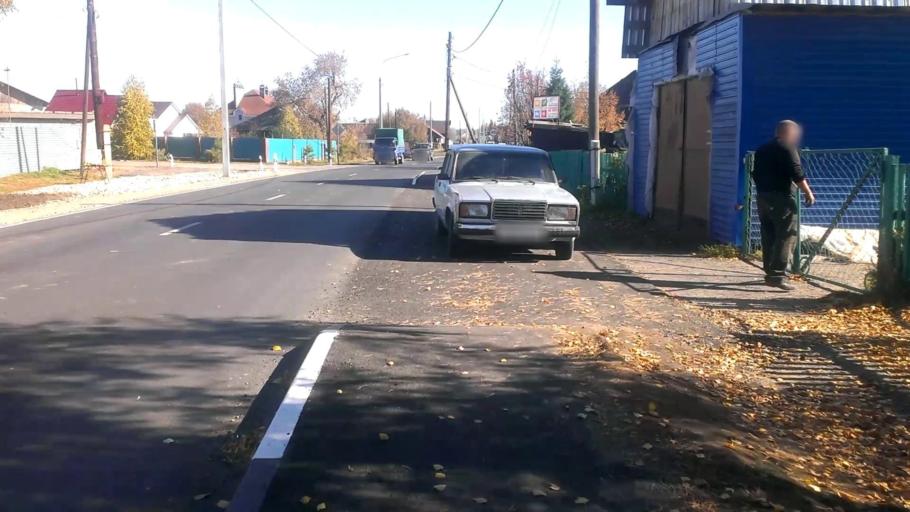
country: RU
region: Altai Krai
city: Sannikovo
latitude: 53.3177
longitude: 83.9476
